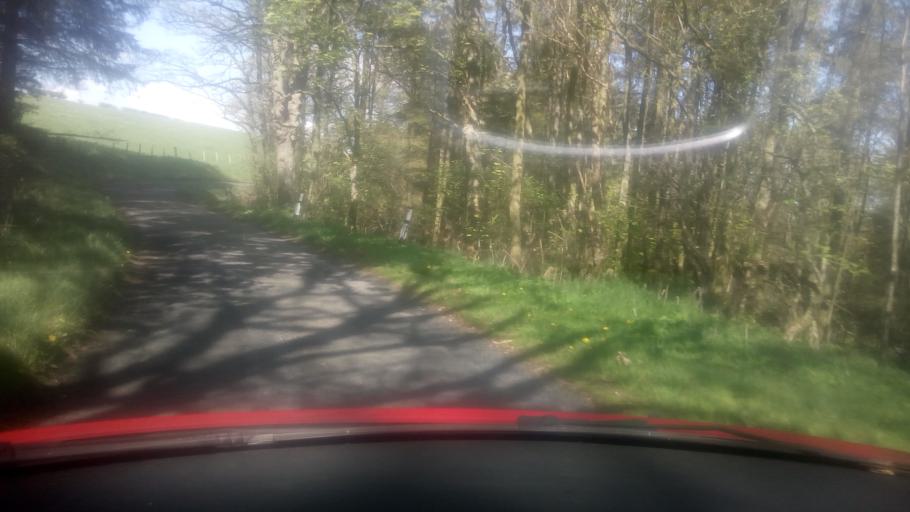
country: GB
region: Scotland
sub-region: The Scottish Borders
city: Hawick
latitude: 55.4260
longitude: -2.7071
